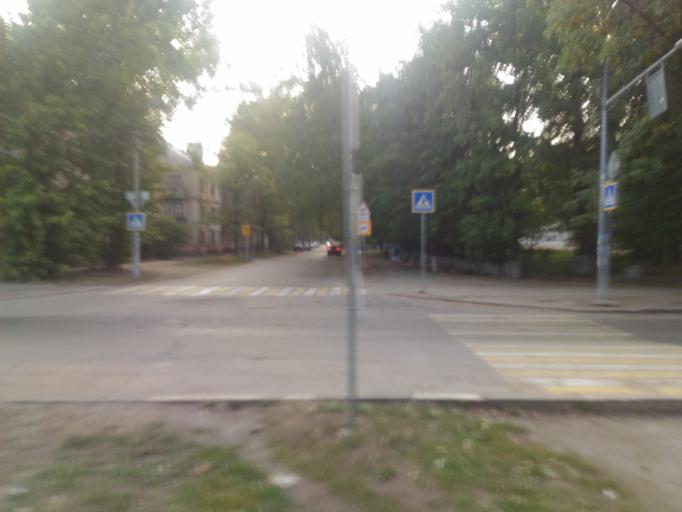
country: RU
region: Ulyanovsk
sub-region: Ulyanovskiy Rayon
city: Ulyanovsk
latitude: 54.2990
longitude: 48.3213
